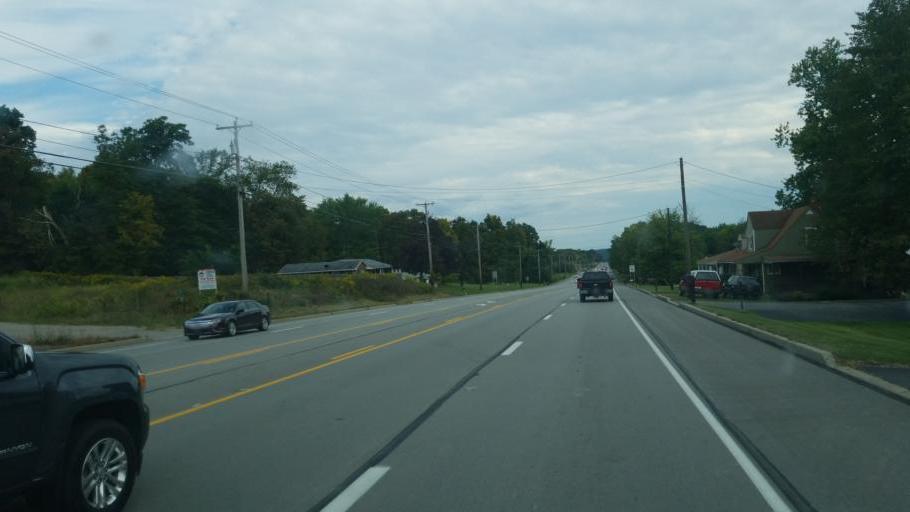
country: US
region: Pennsylvania
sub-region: Mercer County
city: Hermitage
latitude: 41.2068
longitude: -80.4569
